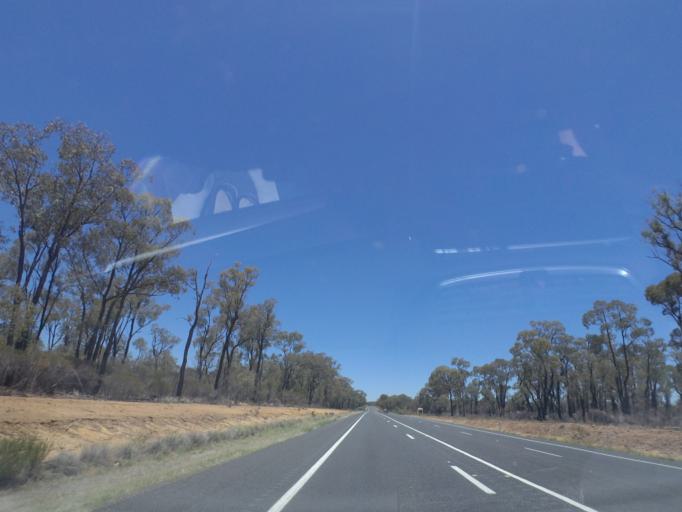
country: AU
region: New South Wales
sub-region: Warrumbungle Shire
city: Coonabarabran
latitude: -30.8779
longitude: 149.4475
